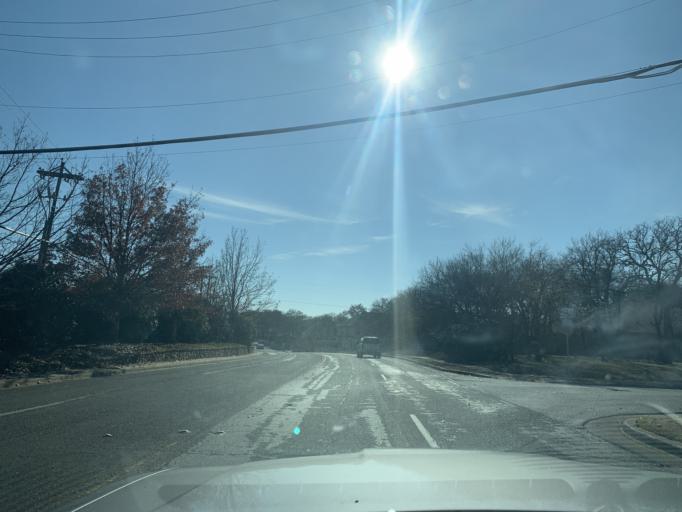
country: US
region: Texas
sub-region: Tarrant County
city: Bedford
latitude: 32.8346
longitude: -97.1421
